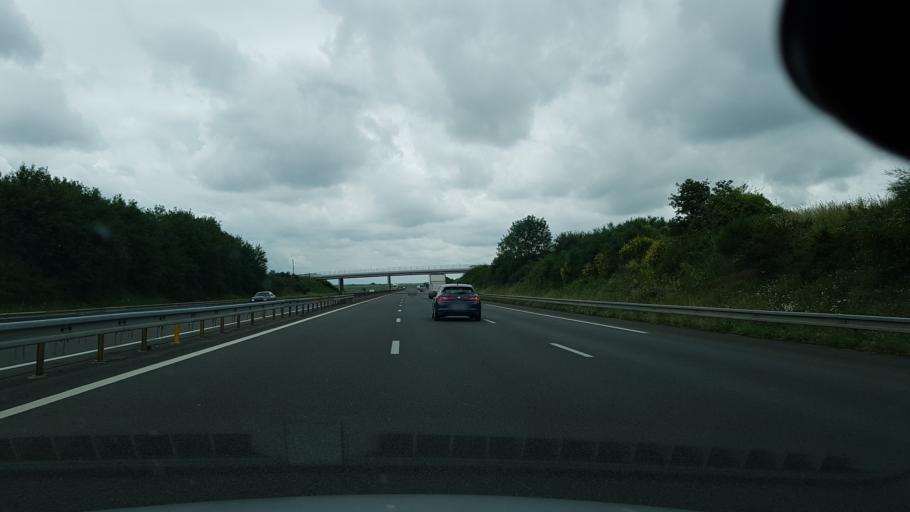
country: FR
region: Centre
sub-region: Departement du Loir-et-Cher
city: Herbault
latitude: 47.5713
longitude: 1.0511
